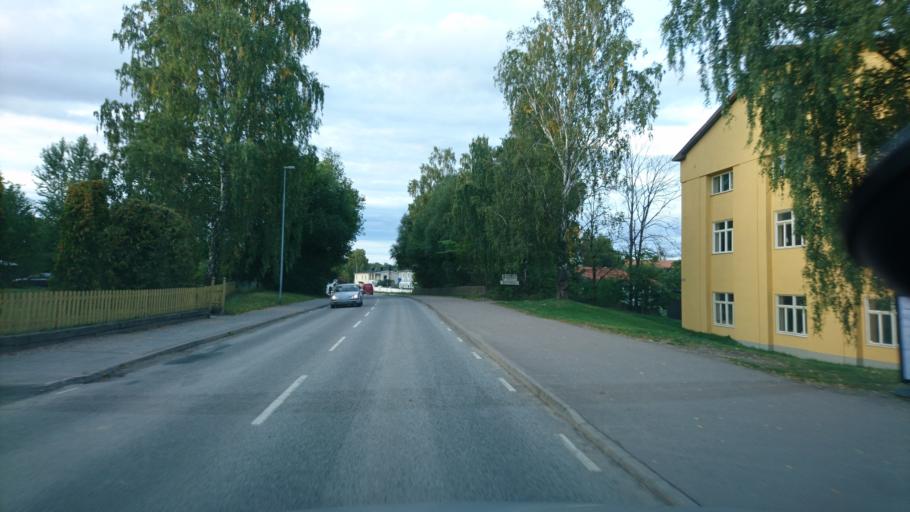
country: SE
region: Soedermanland
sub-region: Strangnas Kommun
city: Stallarholmen
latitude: 59.3595
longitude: 17.2063
